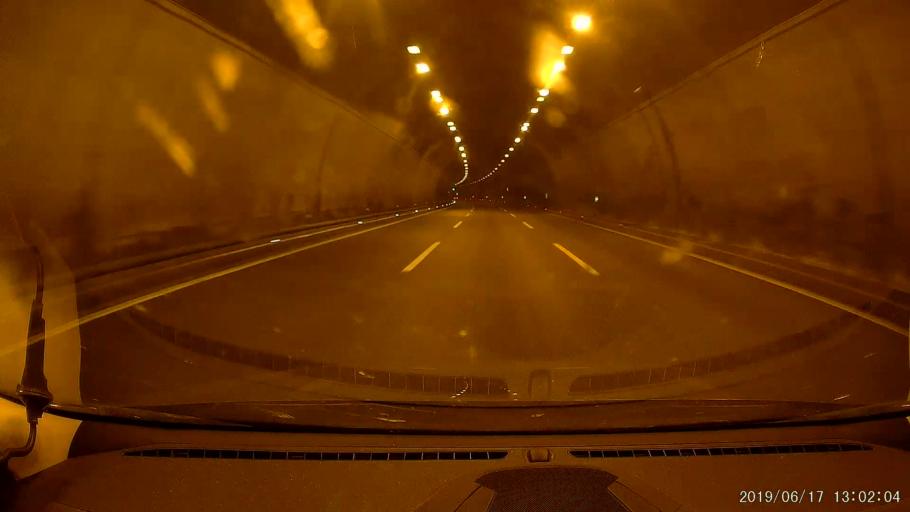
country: TR
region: Duzce
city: Kaynasli
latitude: 40.7370
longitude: 31.4499
